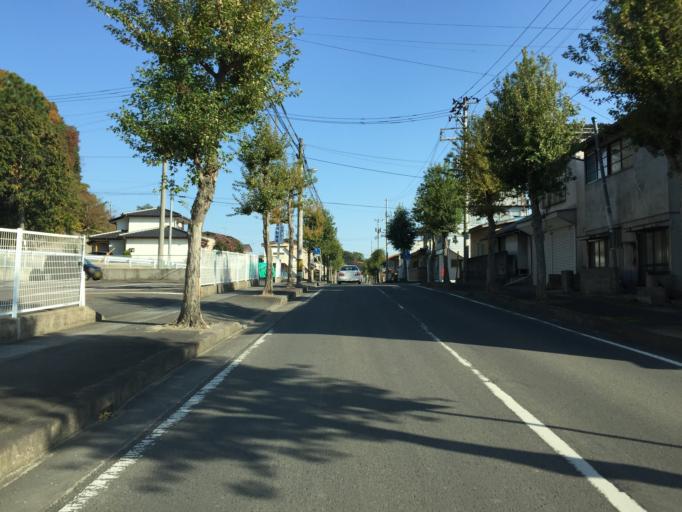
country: JP
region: Fukushima
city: Fukushima-shi
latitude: 37.8332
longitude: 140.4571
